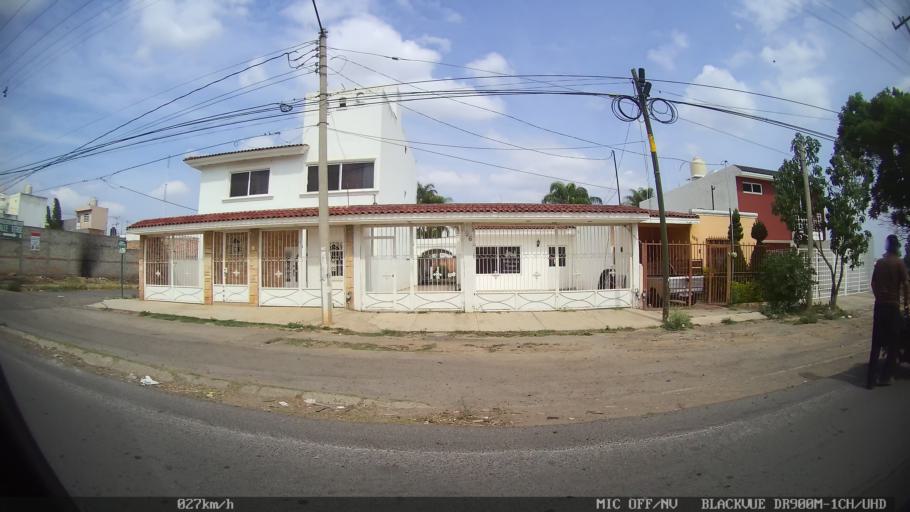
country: MX
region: Jalisco
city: Coyula
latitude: 20.6487
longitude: -103.2217
